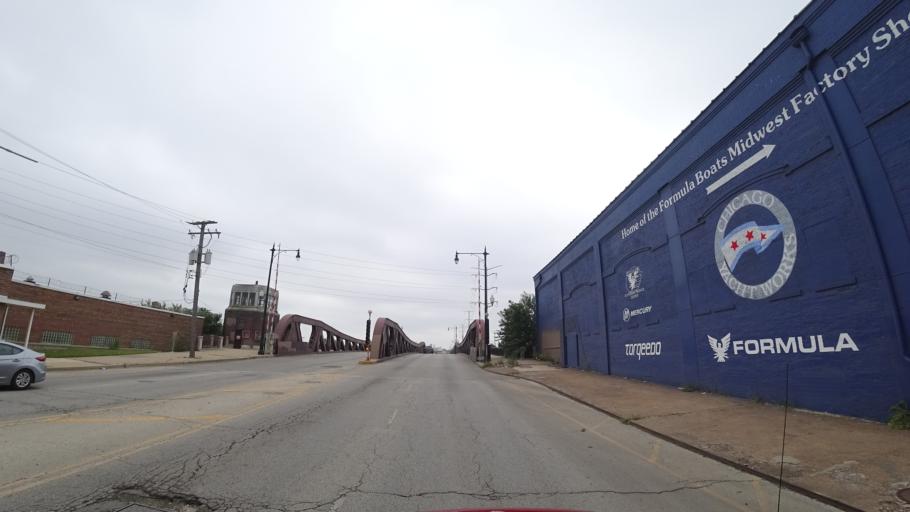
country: US
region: Illinois
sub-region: Cook County
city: Chicago
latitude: 41.8457
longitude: -87.6660
